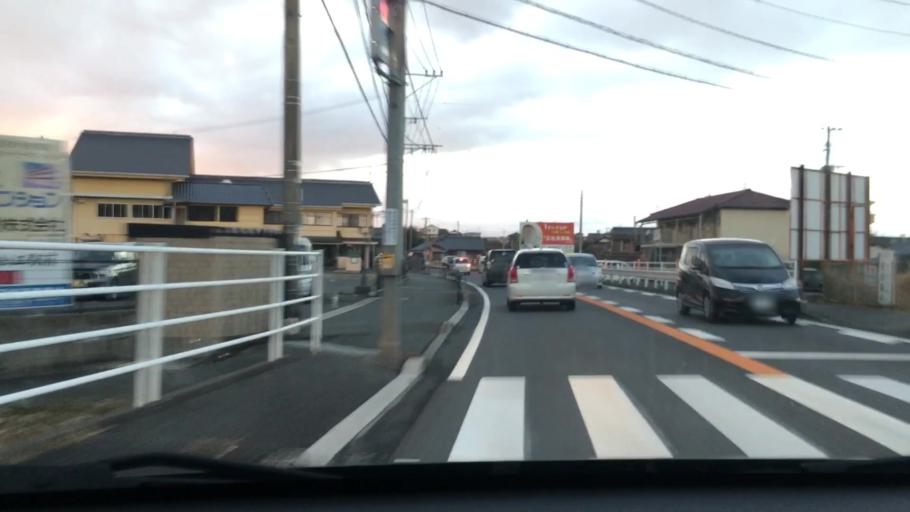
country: JP
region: Fukuoka
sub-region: Buzen-shi
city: Buzen
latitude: 33.6222
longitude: 131.0943
